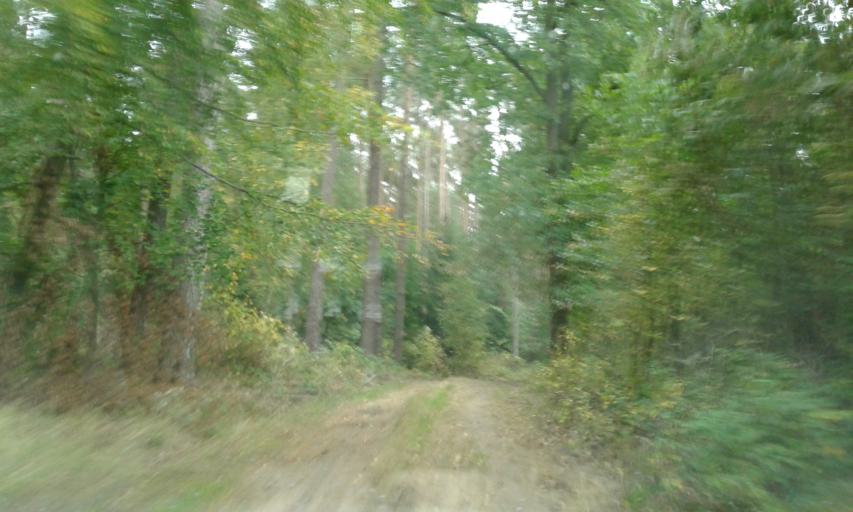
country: PL
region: West Pomeranian Voivodeship
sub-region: Powiat choszczenski
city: Pelczyce
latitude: 53.0922
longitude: 15.2209
